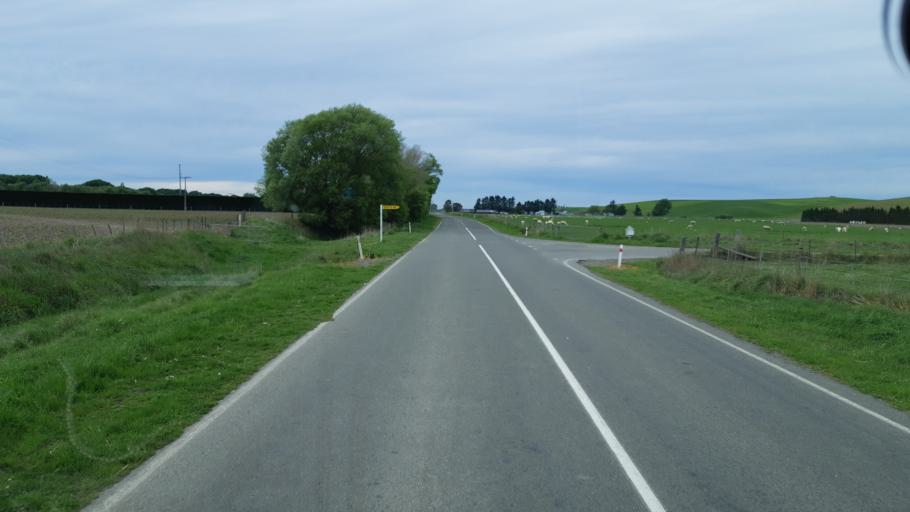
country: NZ
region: Canterbury
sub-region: Timaru District
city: Timaru
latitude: -44.4691
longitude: 171.1293
